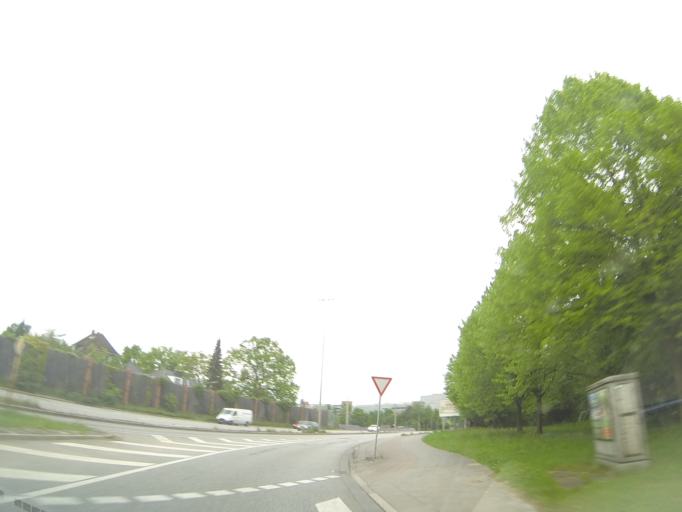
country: DE
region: Hamburg
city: Altona
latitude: 53.5571
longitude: 9.8955
